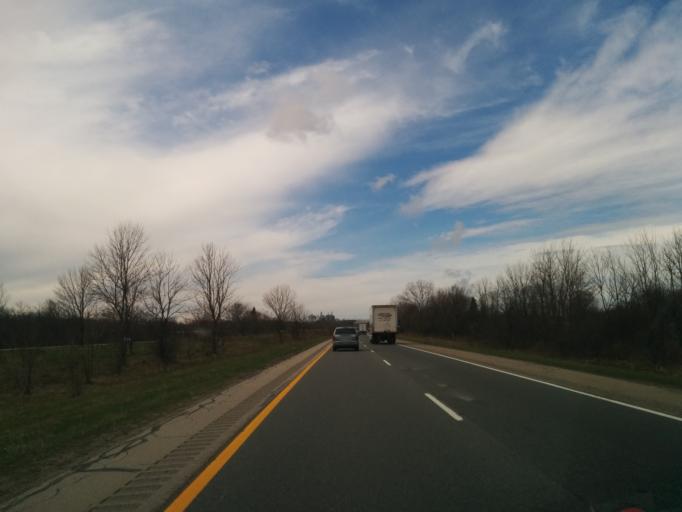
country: US
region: Michigan
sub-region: Ottawa County
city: Zeeland
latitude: 42.8186
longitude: -85.9541
